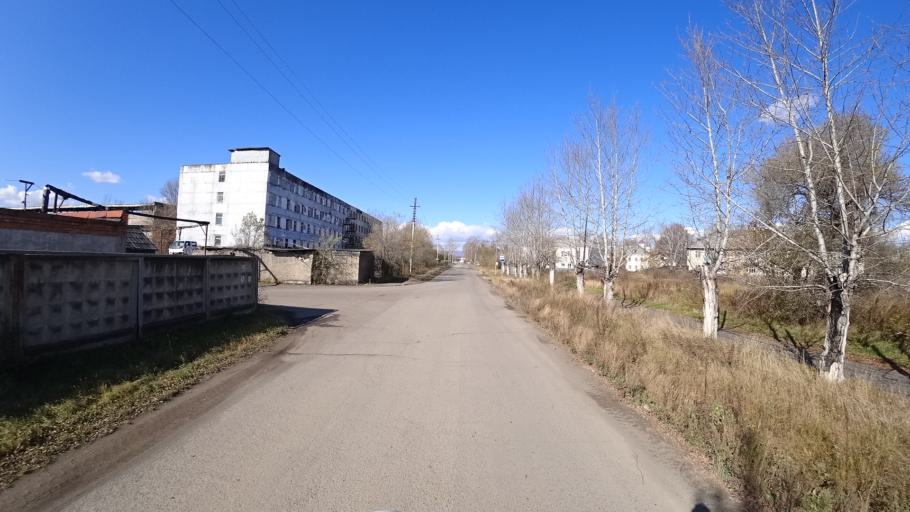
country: RU
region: Khabarovsk Krai
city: Amursk
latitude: 50.0972
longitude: 136.4950
